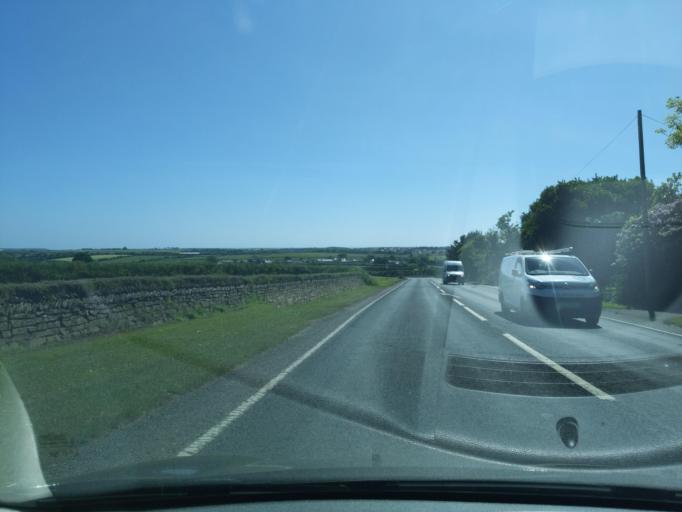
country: GB
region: England
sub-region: Cornwall
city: Wendron
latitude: 50.1181
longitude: -5.2422
